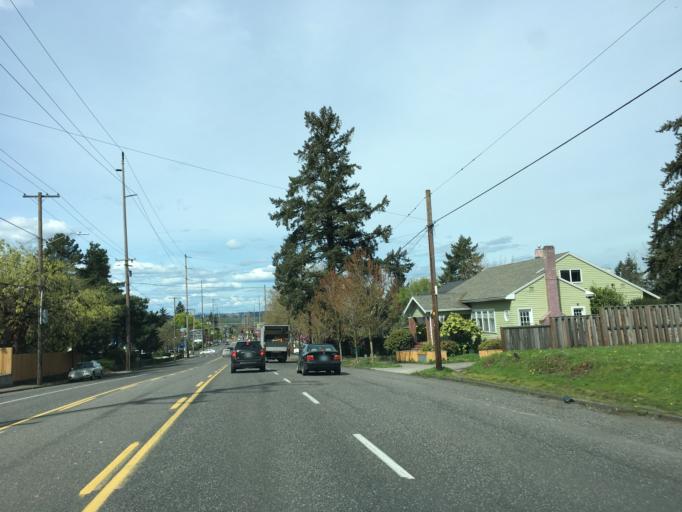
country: US
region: Oregon
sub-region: Multnomah County
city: Lents
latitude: 45.5539
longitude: -122.5577
